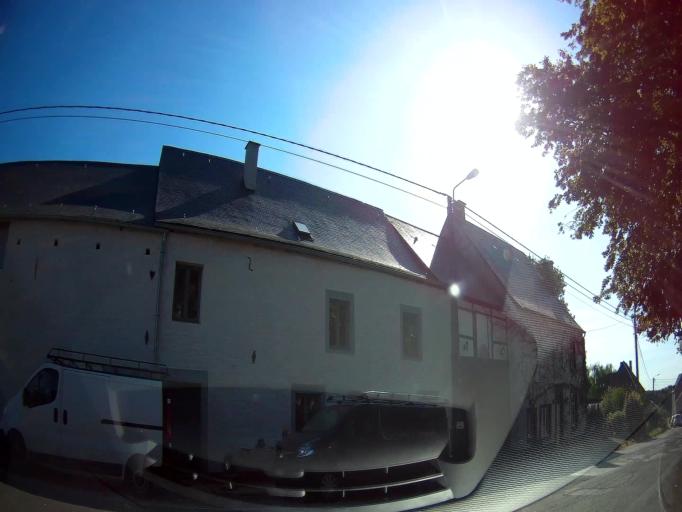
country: BE
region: Wallonia
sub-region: Province de Namur
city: Houyet
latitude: 50.2472
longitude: 4.9902
